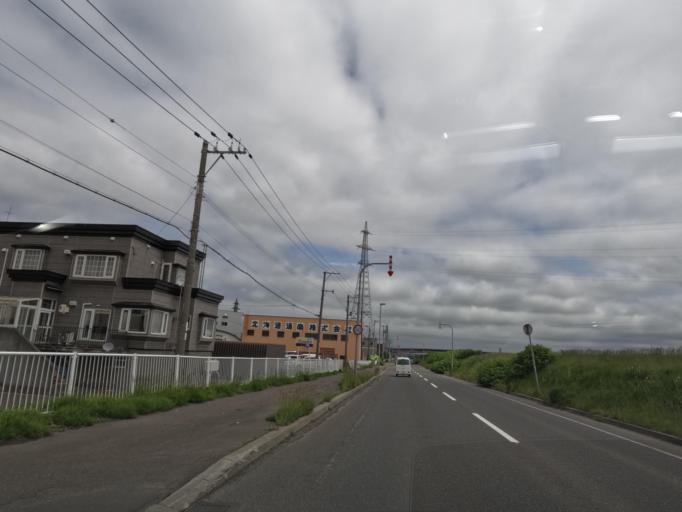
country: JP
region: Hokkaido
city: Sapporo
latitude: 43.0797
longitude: 141.4082
